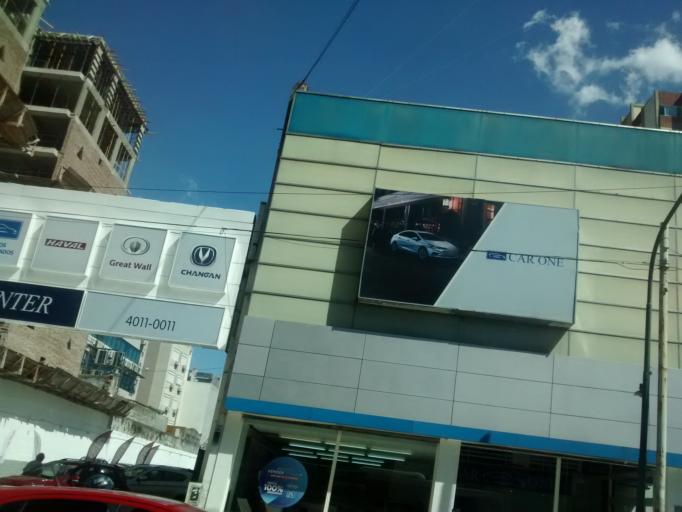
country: AR
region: Buenos Aires F.D.
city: Retiro
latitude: -34.5978
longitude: -58.4180
